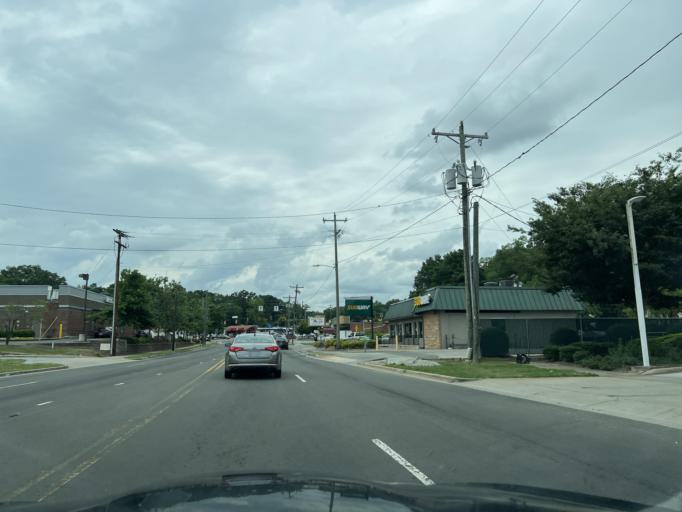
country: US
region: North Carolina
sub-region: Durham County
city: Durham
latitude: 36.0162
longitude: -78.8889
